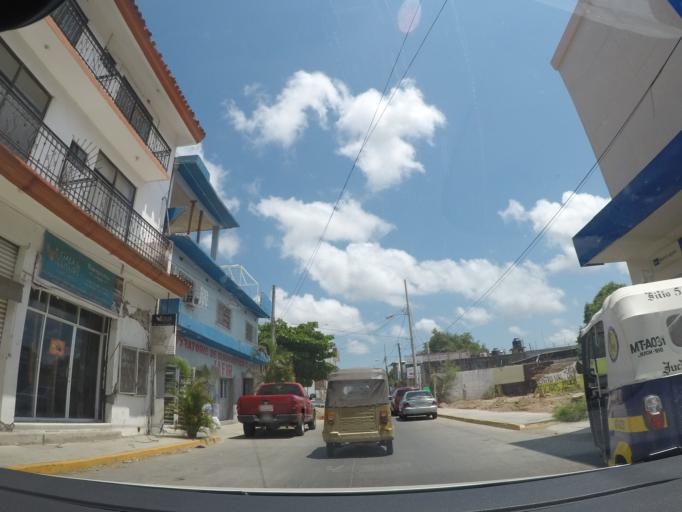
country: MX
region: Oaxaca
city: Juchitan de Zaragoza
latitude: 16.4384
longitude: -95.0222
